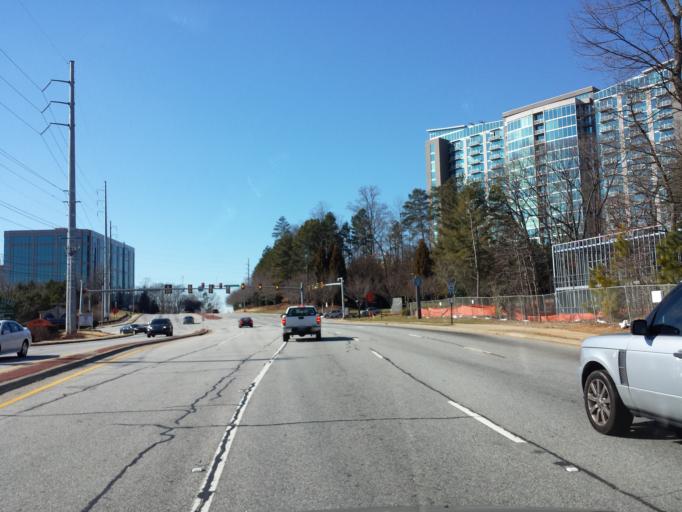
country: US
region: Georgia
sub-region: Cobb County
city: Vinings
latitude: 33.9025
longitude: -84.4546
